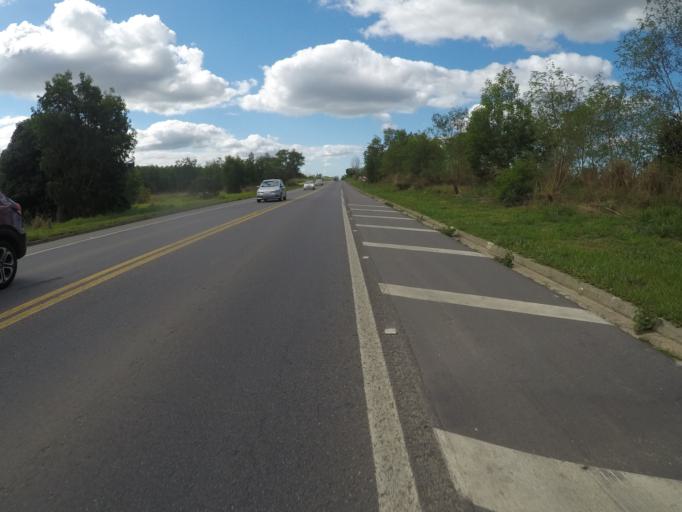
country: BR
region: Espirito Santo
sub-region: Linhares
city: Linhares
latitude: -19.1758
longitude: -40.0907
